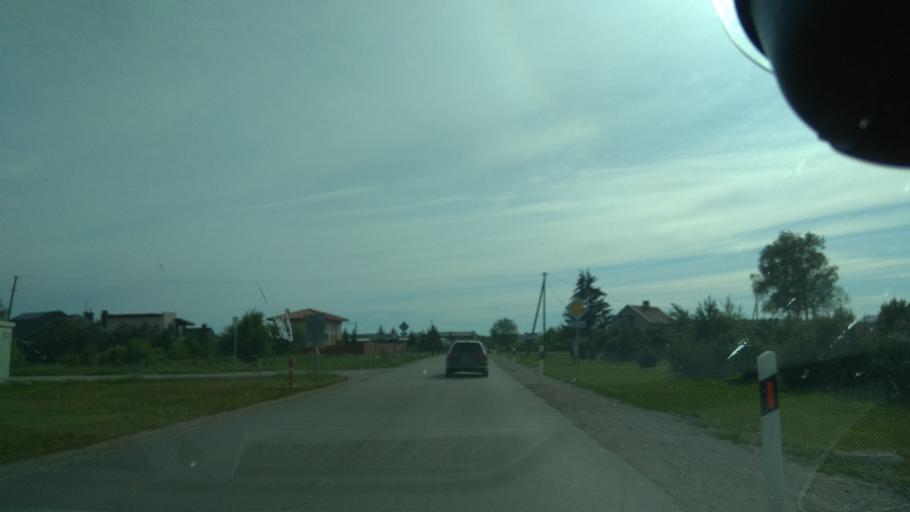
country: LT
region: Klaipedos apskritis
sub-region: Klaipeda
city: Klaipeda
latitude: 55.7549
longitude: 21.1823
